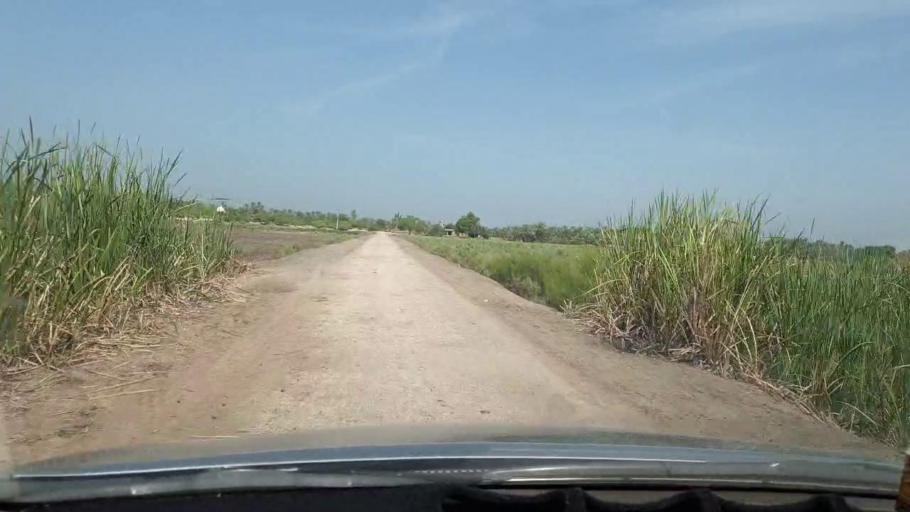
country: PK
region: Sindh
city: Khairpur
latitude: 27.4716
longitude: 68.7442
